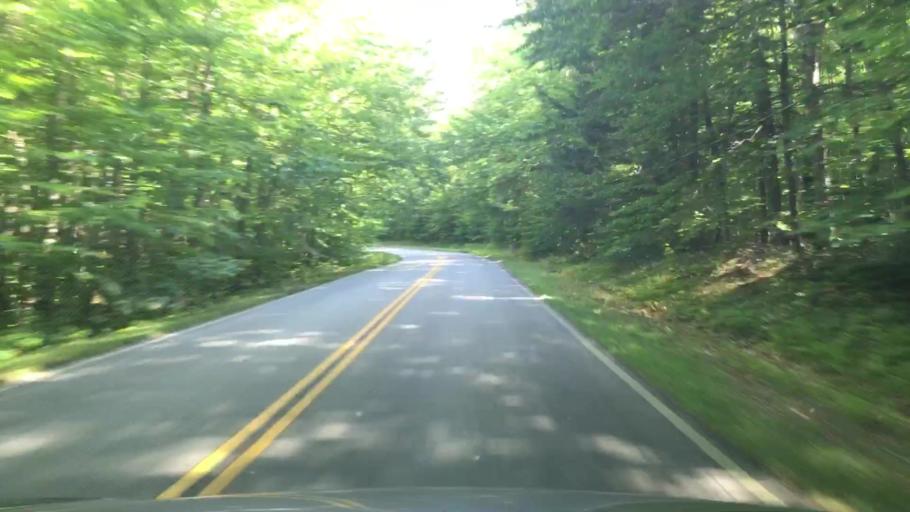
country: US
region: New Hampshire
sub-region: Carroll County
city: North Conway
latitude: 44.0634
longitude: -71.2818
